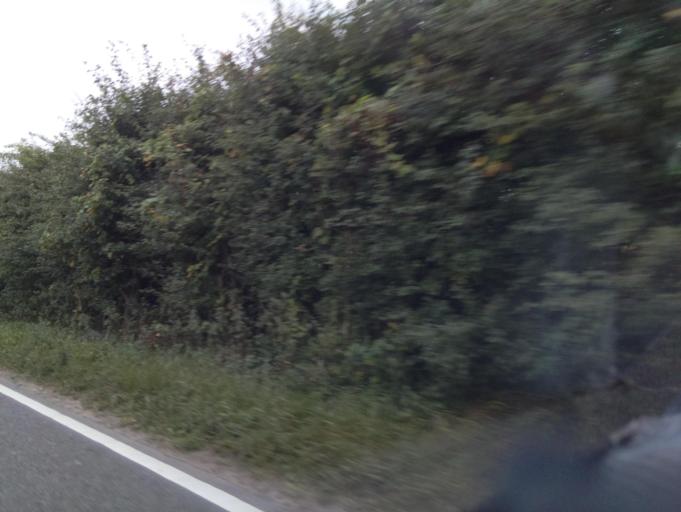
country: GB
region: England
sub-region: Shropshire
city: Astley
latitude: 52.7606
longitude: -2.6911
